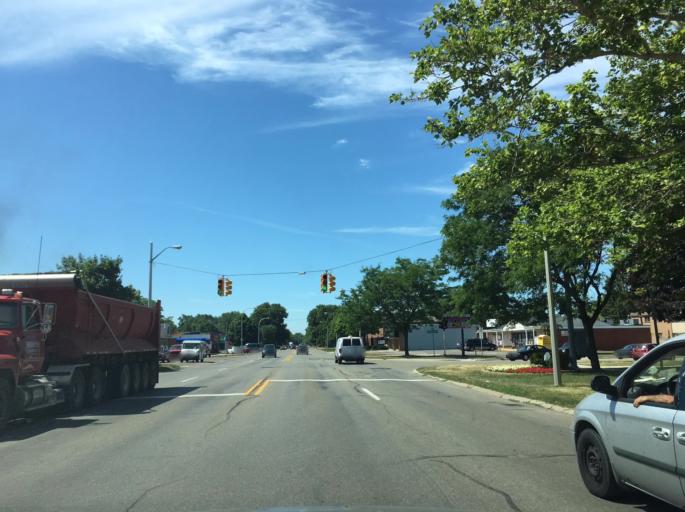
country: US
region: Michigan
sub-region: Wayne County
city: Allen Park
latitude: 42.2499
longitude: -83.2180
